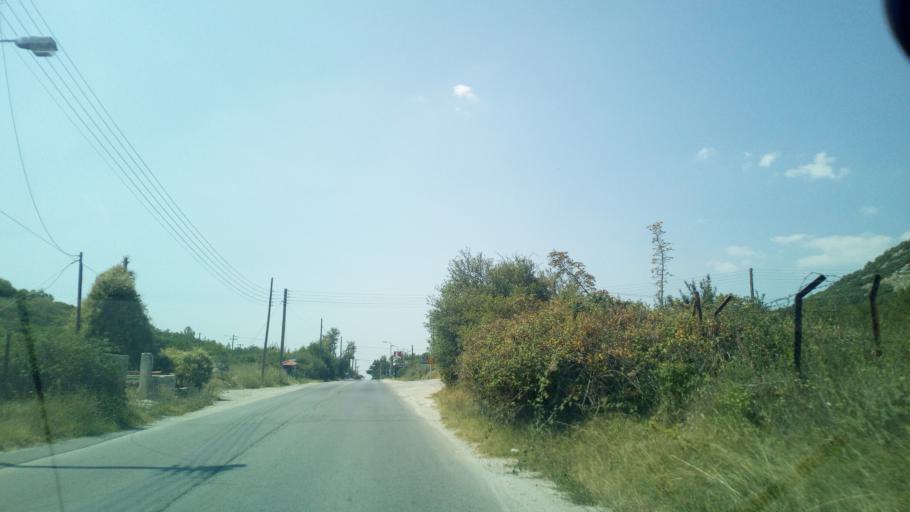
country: GR
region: Central Macedonia
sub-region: Nomos Thessalonikis
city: Asvestochori
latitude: 40.6263
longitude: 23.0600
